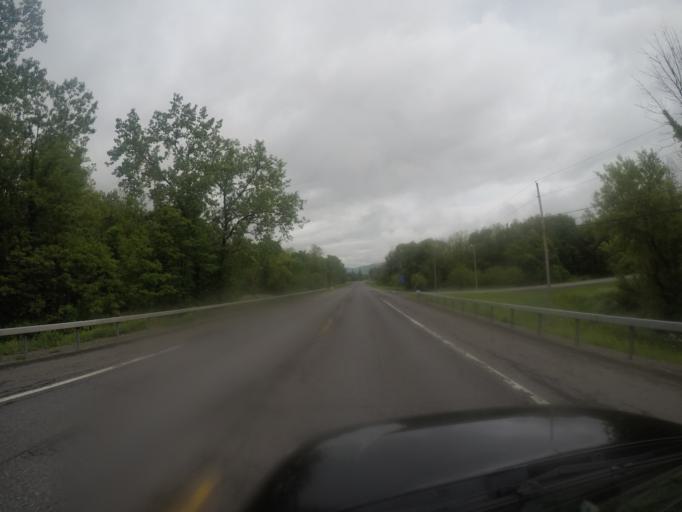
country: US
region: New York
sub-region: Ulster County
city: Shokan
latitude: 42.0243
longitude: -74.2704
